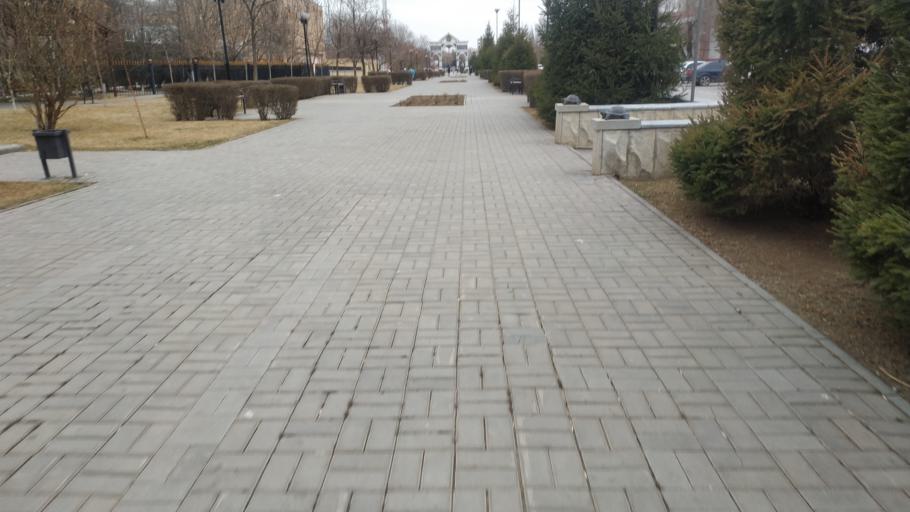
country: RU
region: Astrakhan
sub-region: Gorod Astrakhan'
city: Astrakhan'
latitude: 46.3465
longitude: 48.0174
